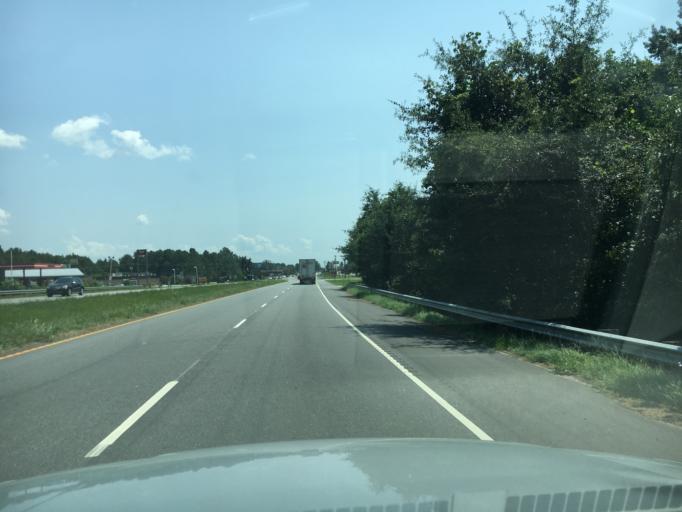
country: US
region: South Carolina
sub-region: Anderson County
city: Pendleton
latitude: 34.6369
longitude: -82.7859
